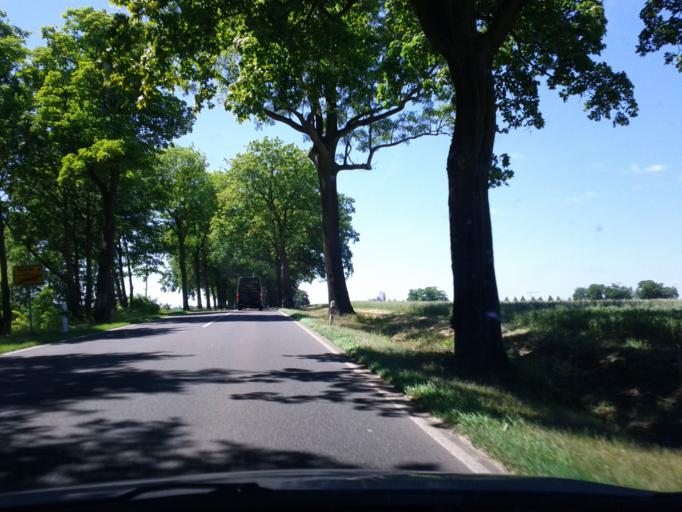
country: DE
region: Brandenburg
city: Rehfelde
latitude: 52.4809
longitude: 13.8950
